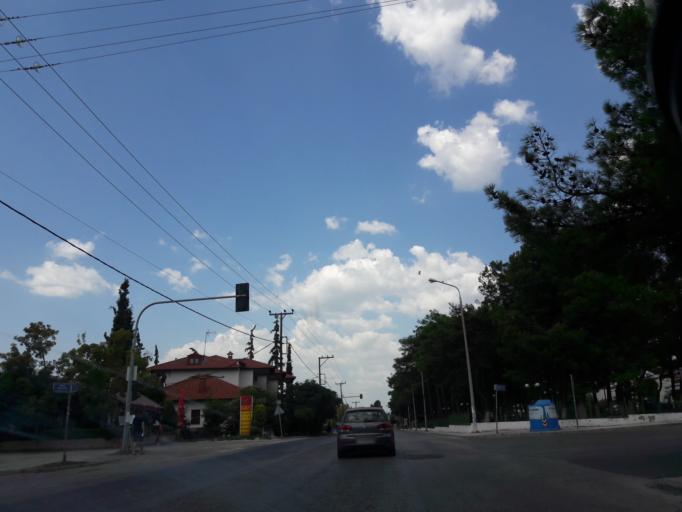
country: GR
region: Central Macedonia
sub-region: Nomos Thessalonikis
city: Thermi
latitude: 40.5245
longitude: 23.0500
